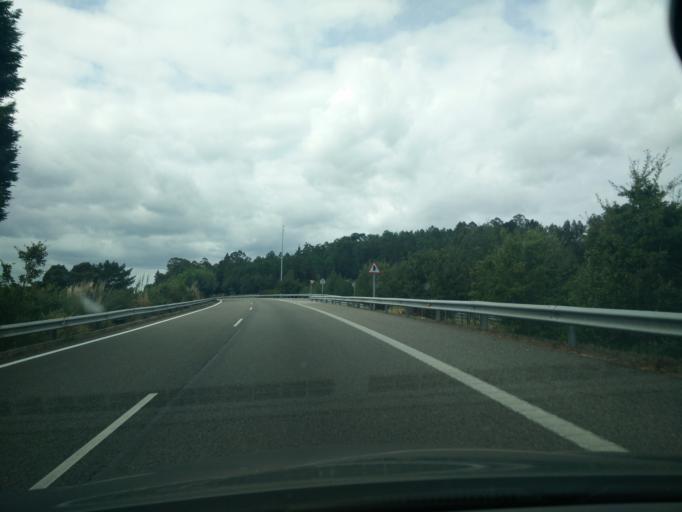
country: ES
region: Galicia
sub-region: Provincia da Coruna
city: Oleiros
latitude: 43.2888
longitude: -8.2824
